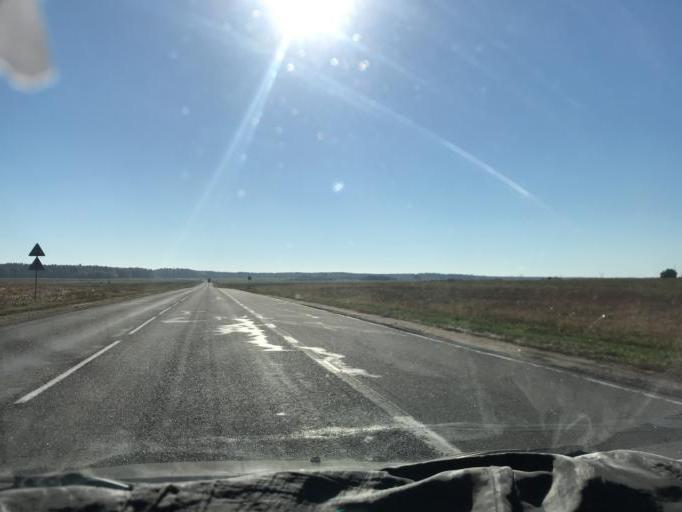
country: BY
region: Mogilev
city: Babruysk
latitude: 53.0698
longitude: 29.0762
